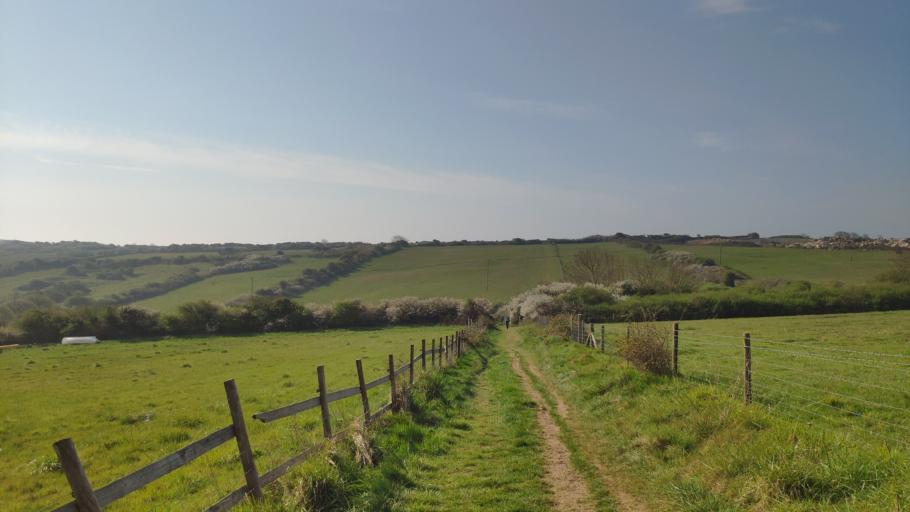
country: GB
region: England
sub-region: Dorset
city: Swanage
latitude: 50.6011
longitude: -1.9665
